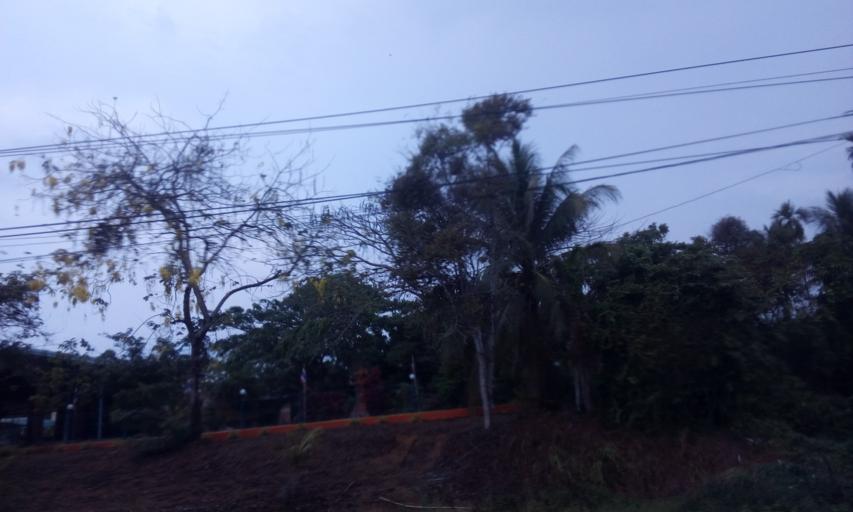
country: TH
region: Trat
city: Khao Saming
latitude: 12.3613
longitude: 102.3839
